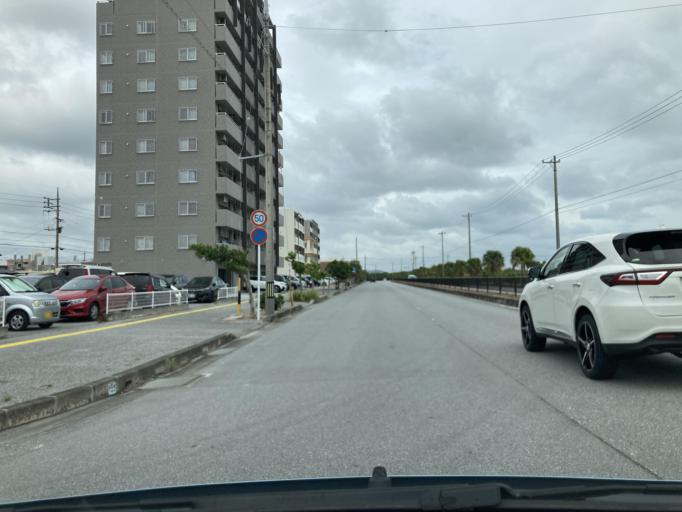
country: JP
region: Okinawa
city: Ginowan
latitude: 26.2071
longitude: 127.7629
